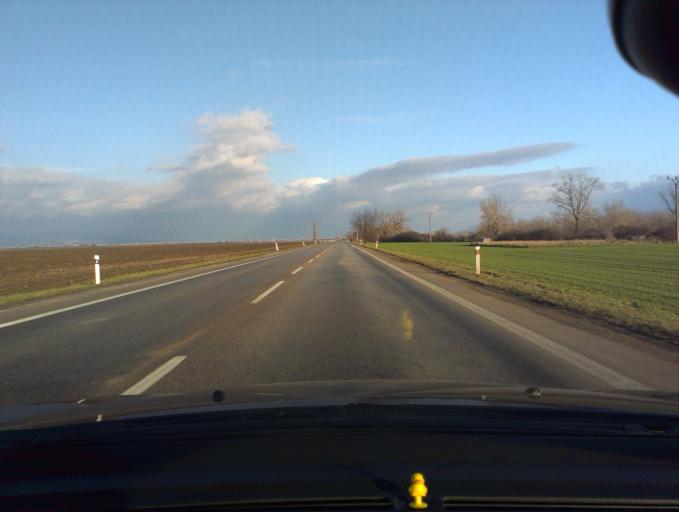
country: SK
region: Trnavsky
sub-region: Okres Trnava
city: Piestany
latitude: 48.6206
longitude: 17.8368
